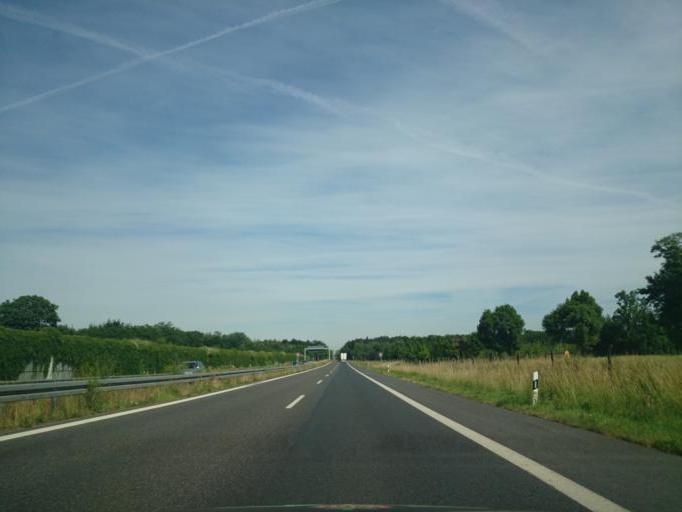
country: DE
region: Berlin
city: Lichtenrade
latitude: 52.3720
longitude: 13.4211
